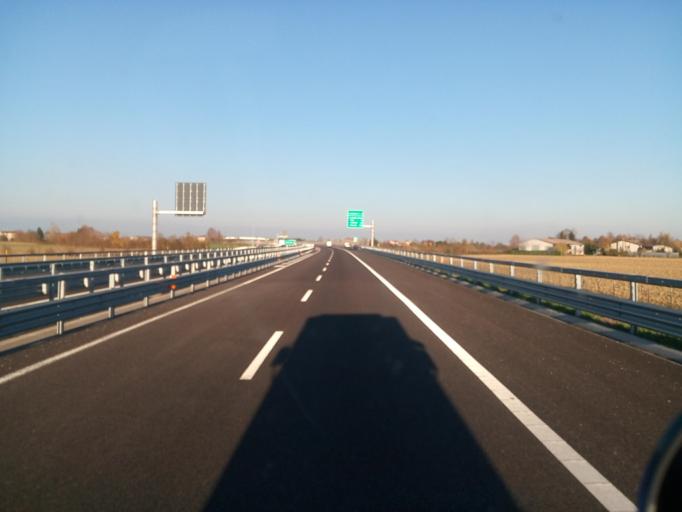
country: IT
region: Veneto
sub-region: Provincia di Padova
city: Bastia
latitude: 45.3956
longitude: 11.6239
